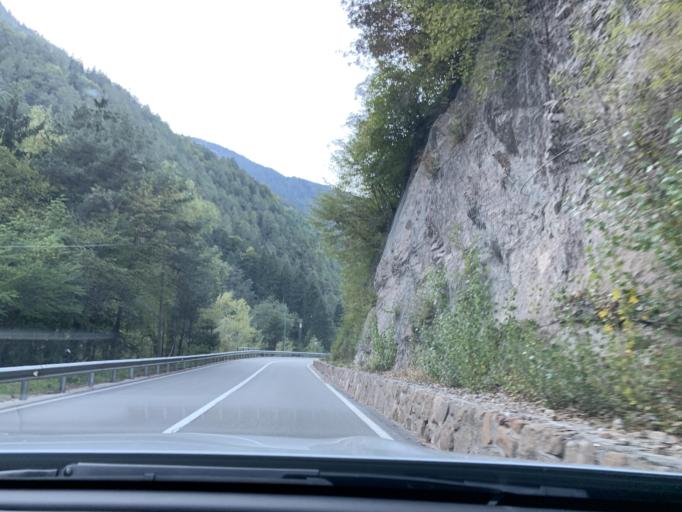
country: IT
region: Trentino-Alto Adige
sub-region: Bolzano
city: Cornedo All'Isarco
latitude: 46.4627
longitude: 11.4149
